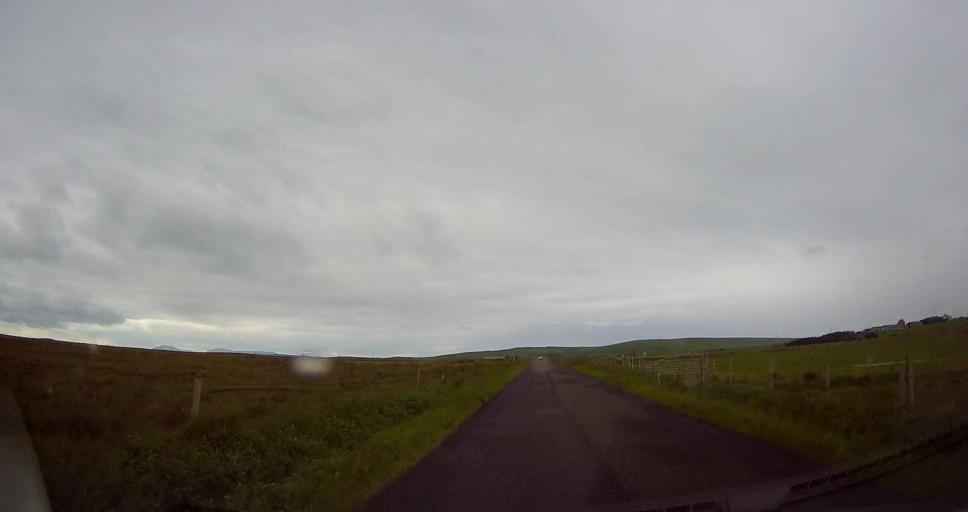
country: GB
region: Scotland
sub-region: Orkney Islands
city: Stromness
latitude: 59.1018
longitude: -3.2613
